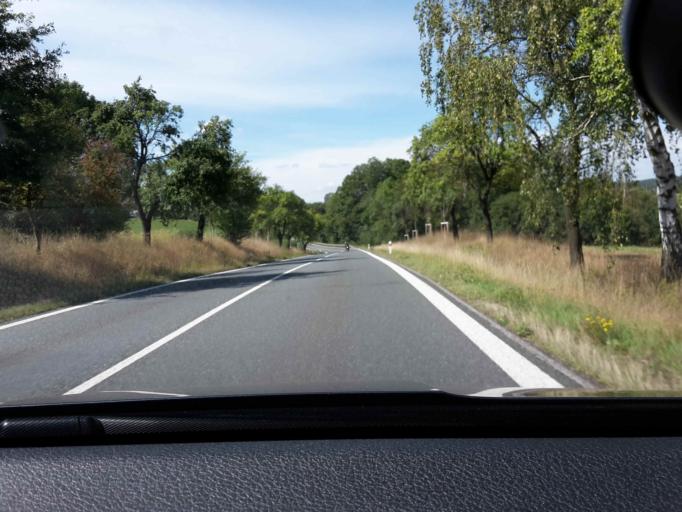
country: CZ
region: Jihocesky
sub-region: Okres Jindrichuv Hradec
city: Jindrichuv Hradec
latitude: 49.1585
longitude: 14.9639
